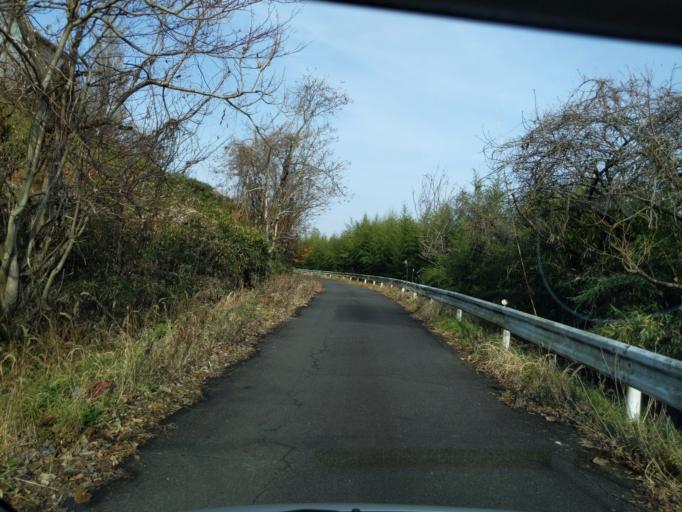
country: JP
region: Miyagi
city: Wakuya
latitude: 38.6983
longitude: 141.1479
